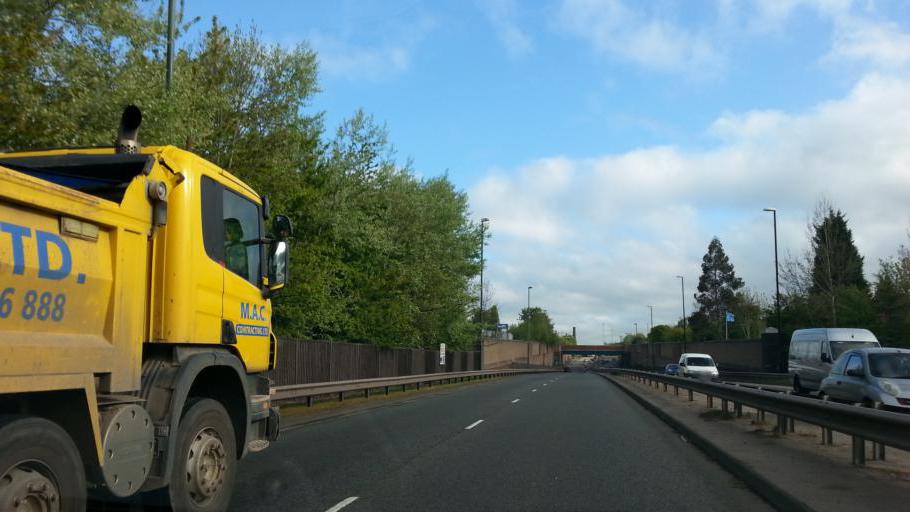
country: GB
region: England
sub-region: Coventry
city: Coventry
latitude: 52.4175
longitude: -1.4870
